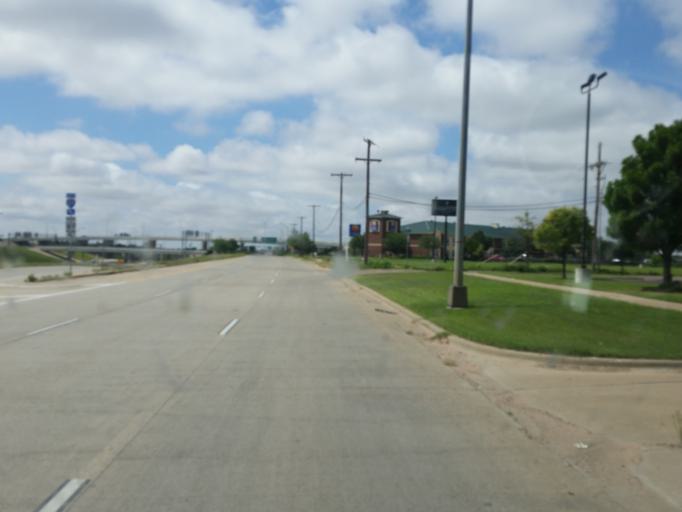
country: US
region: Texas
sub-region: Lubbock County
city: Lubbock
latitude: 33.5420
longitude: -101.8457
